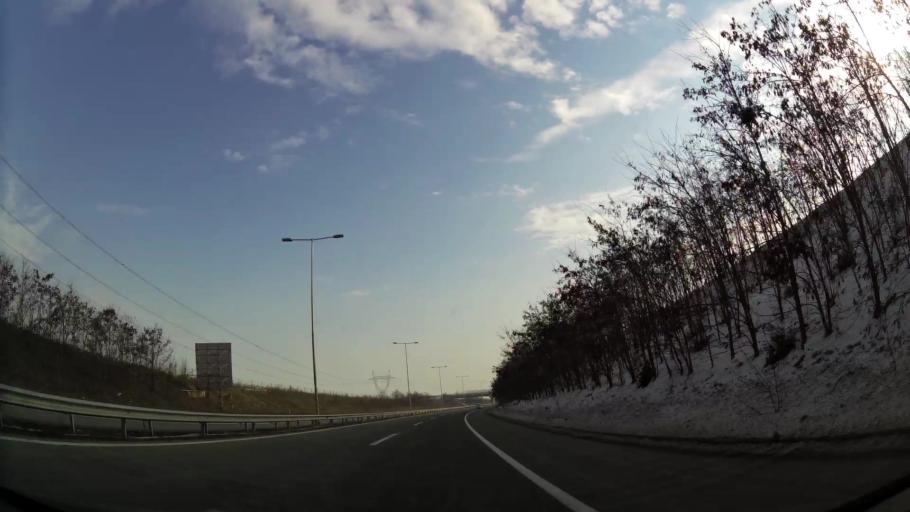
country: MK
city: Creshevo
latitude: 42.0327
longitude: 21.5258
